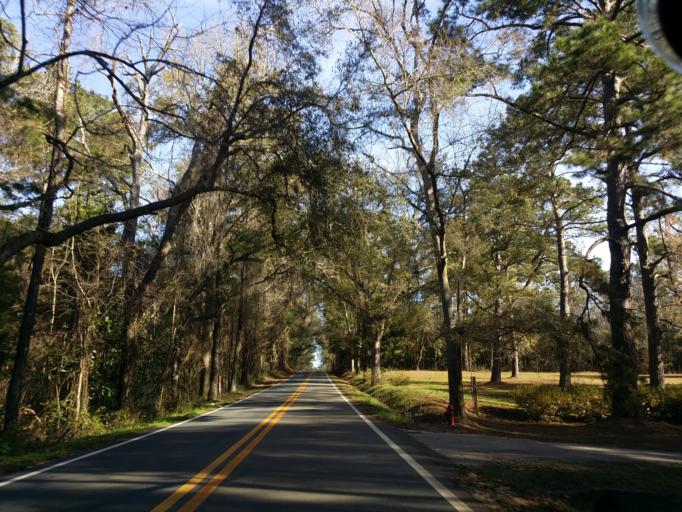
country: US
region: Florida
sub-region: Leon County
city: Woodville
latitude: 30.3886
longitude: -84.1553
